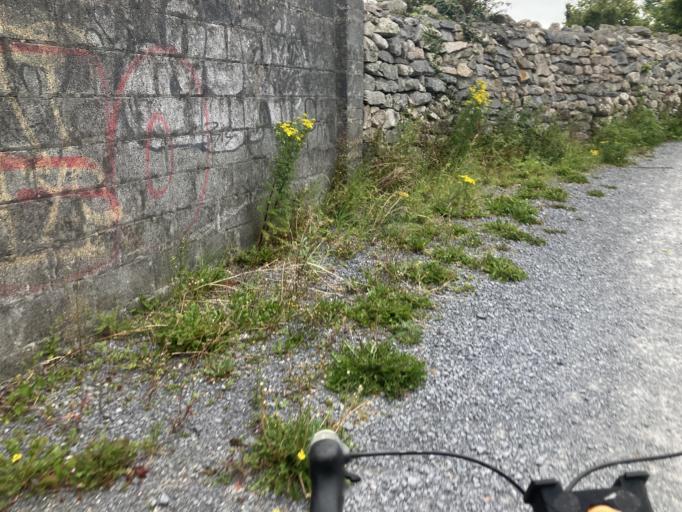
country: IE
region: Connaught
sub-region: County Galway
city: Gaillimh
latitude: 53.2691
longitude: -9.0947
